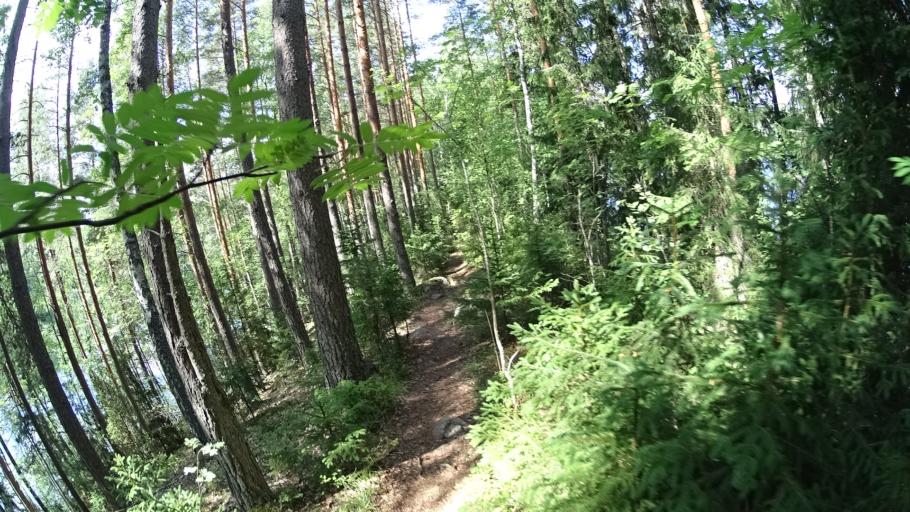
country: FI
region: Haeme
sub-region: Forssa
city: Tammela
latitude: 60.7723
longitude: 23.8539
